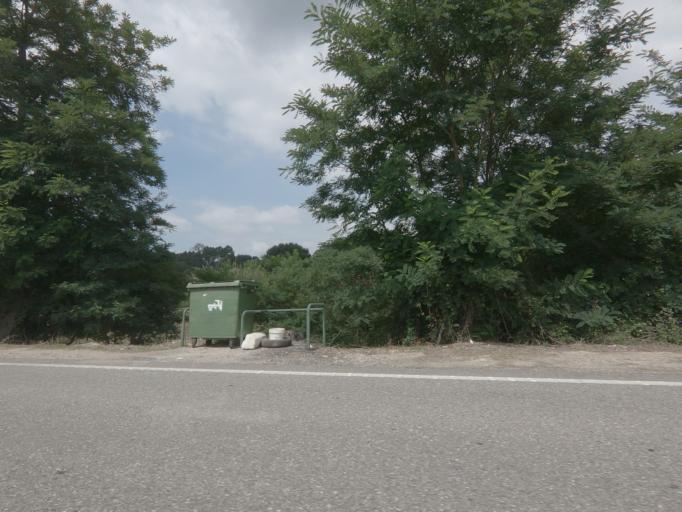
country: PT
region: Viana do Castelo
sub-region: Valenca
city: Valenca
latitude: 42.0321
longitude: -8.6682
